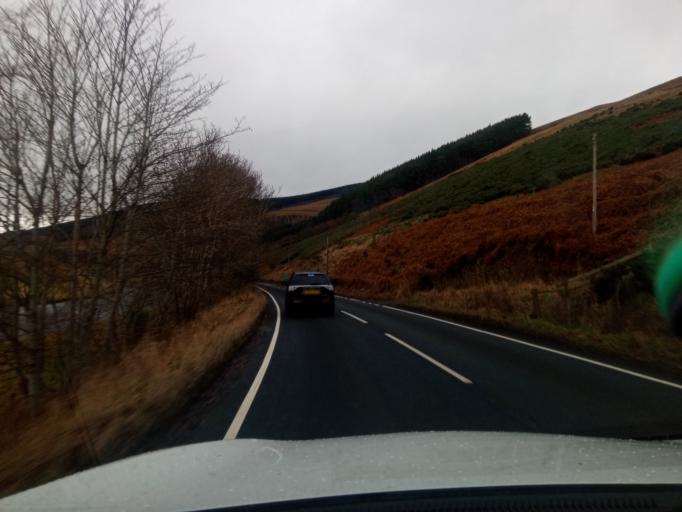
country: GB
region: Scotland
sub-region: The Scottish Borders
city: Innerleithen
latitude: 55.6291
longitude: -2.9815
